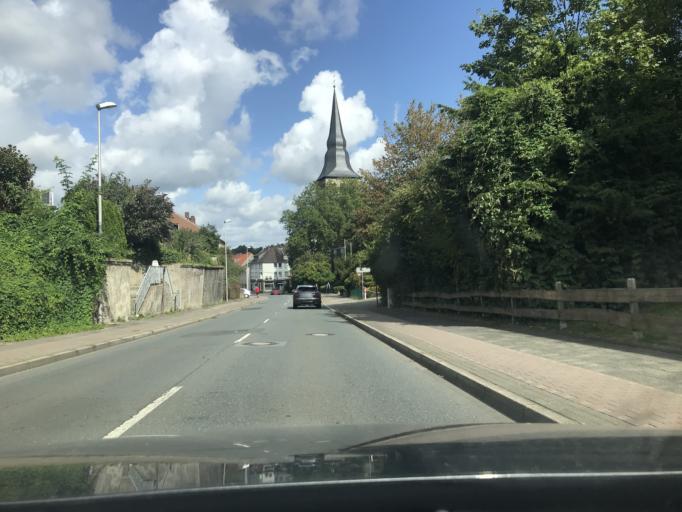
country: DE
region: North Rhine-Westphalia
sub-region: Regierungsbezirk Dusseldorf
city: Erkrath
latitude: 51.2206
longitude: 6.9131
